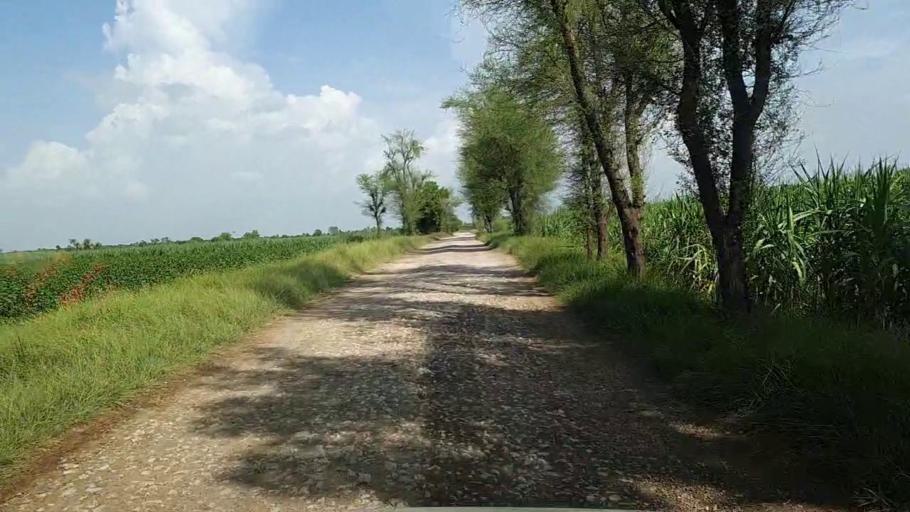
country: PK
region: Sindh
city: Bhiria
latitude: 26.9039
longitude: 68.2251
